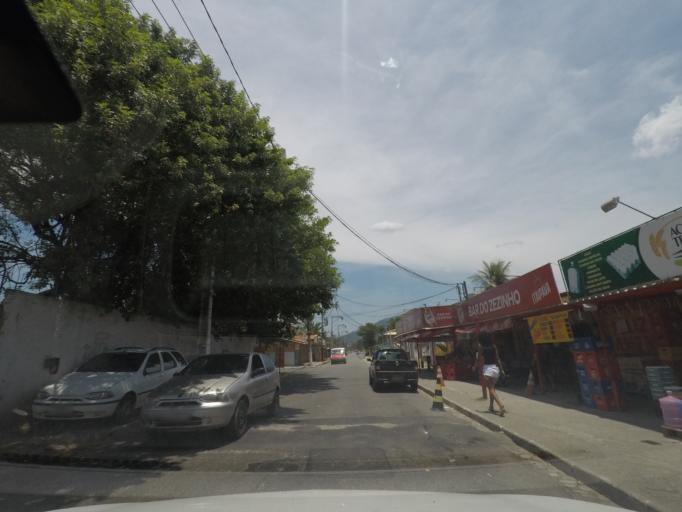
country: BR
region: Rio de Janeiro
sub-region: Marica
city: Marica
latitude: -22.9097
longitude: -42.8283
